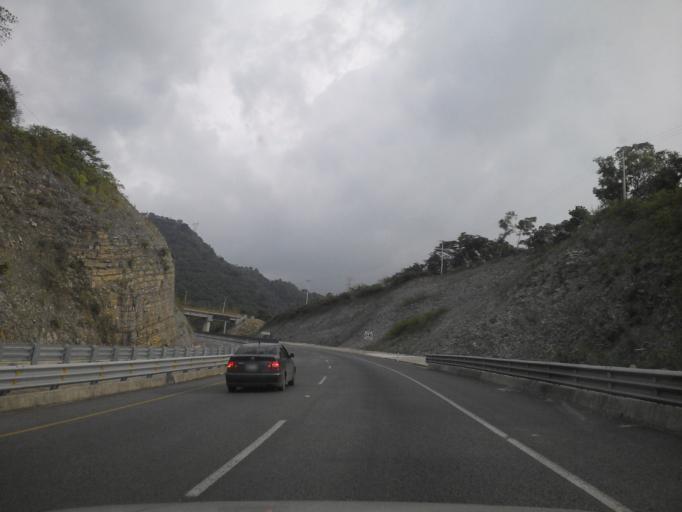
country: MX
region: Puebla
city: Xicotepec de Juarez
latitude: 20.3022
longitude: -97.9700
